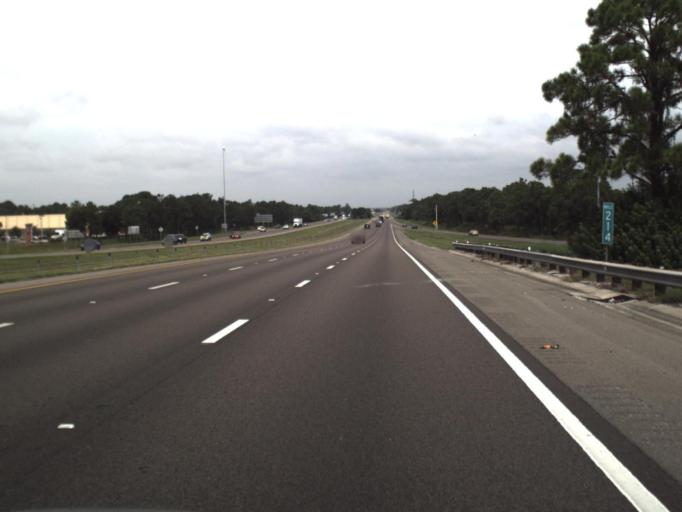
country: US
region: Florida
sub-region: Sarasota County
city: The Meadows
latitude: 27.3898
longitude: -82.4489
